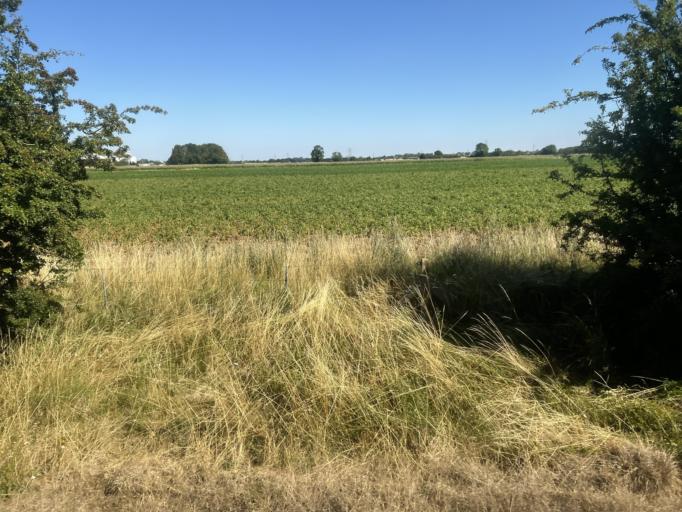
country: GB
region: England
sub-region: Lincolnshire
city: Sleaford
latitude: 52.9934
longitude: -0.3799
